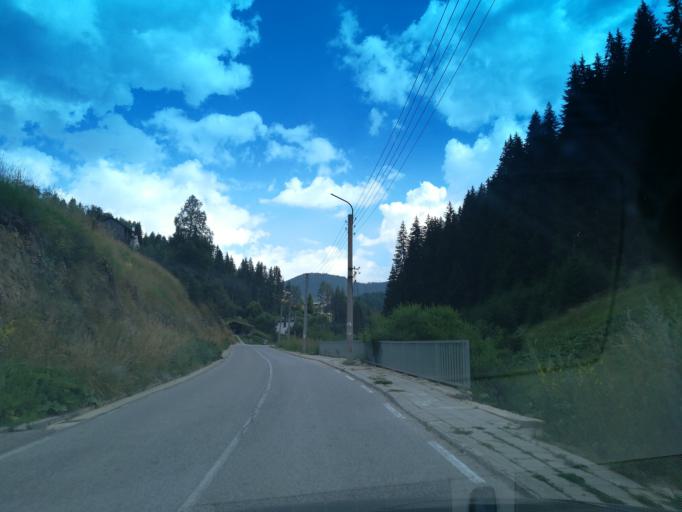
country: BG
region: Smolyan
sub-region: Obshtina Chepelare
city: Chepelare
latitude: 41.6568
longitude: 24.6332
